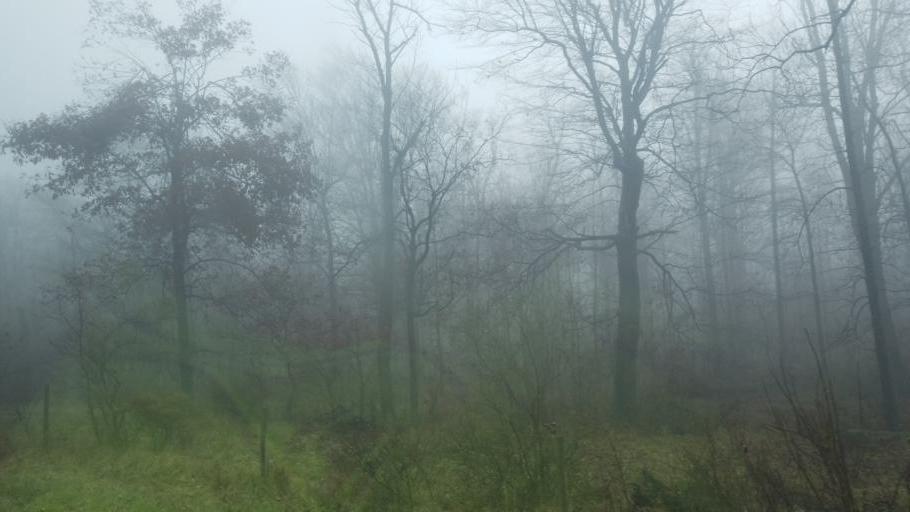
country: US
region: Ohio
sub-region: Champaign County
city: North Lewisburg
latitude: 40.2994
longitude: -83.6319
